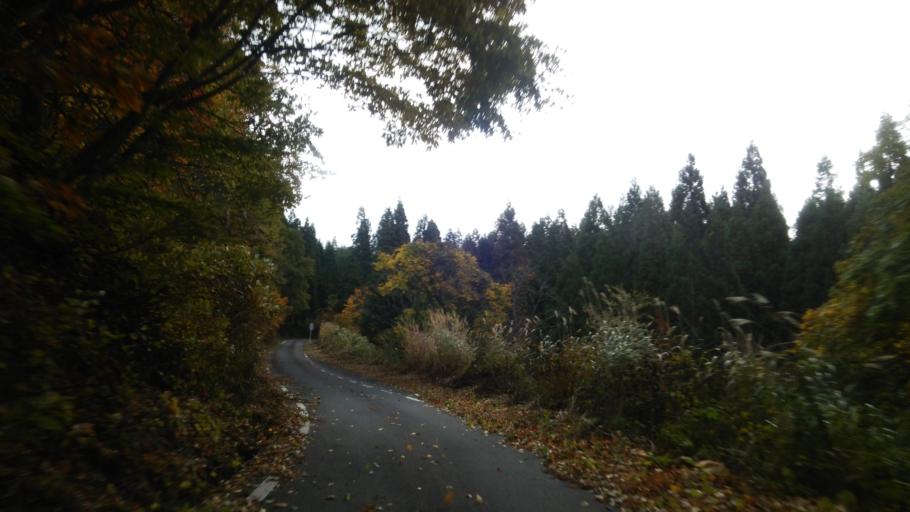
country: JP
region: Fukushima
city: Kitakata
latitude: 37.3842
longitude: 139.7291
